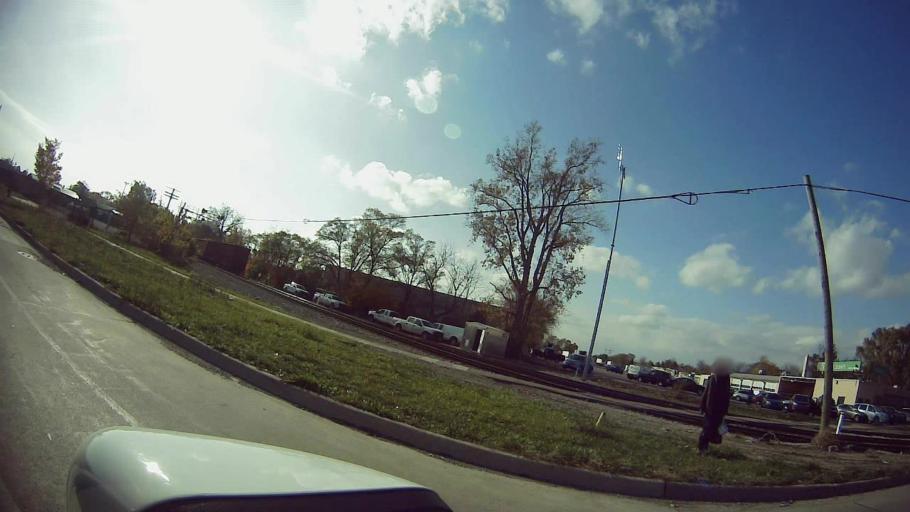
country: US
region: Michigan
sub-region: Macomb County
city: Warren
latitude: 42.4362
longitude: -83.0146
